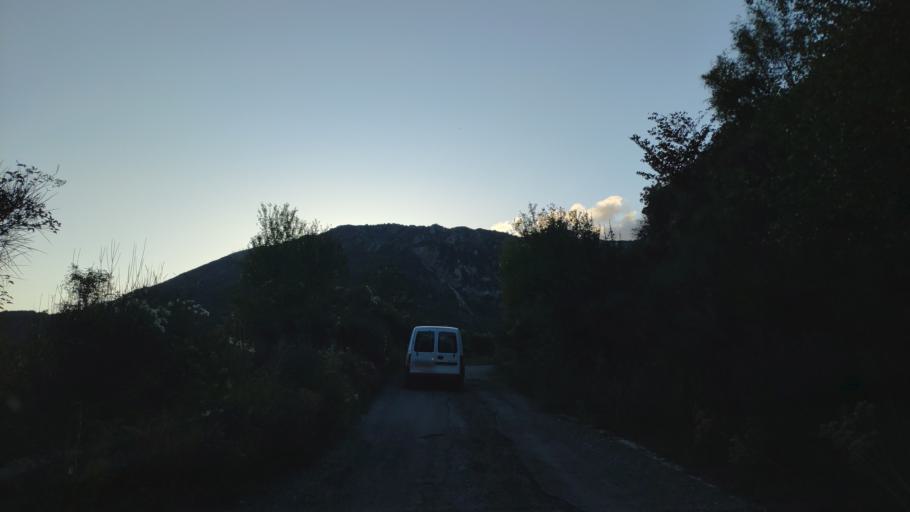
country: GR
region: Peloponnese
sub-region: Nomos Arkadias
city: Dimitsana
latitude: 37.5768
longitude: 22.0487
